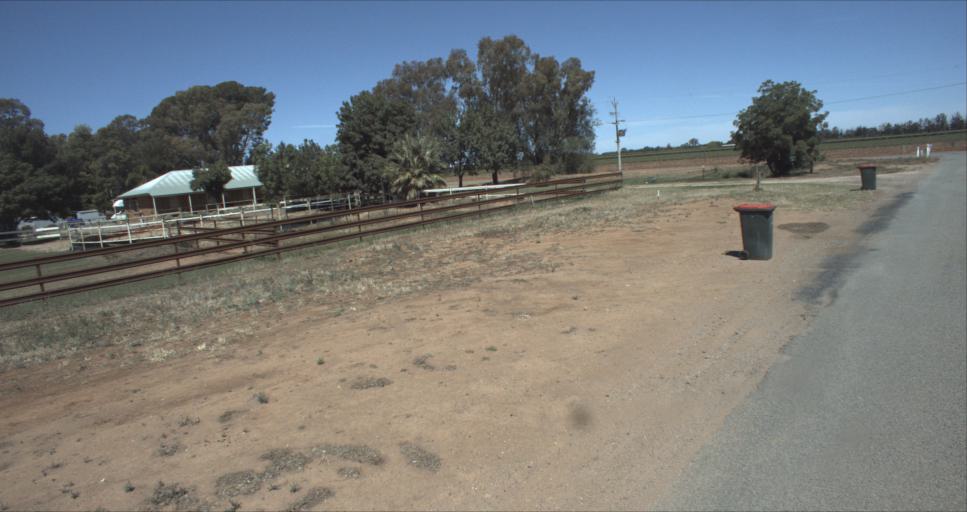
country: AU
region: New South Wales
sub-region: Leeton
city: Leeton
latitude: -34.5304
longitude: 146.3332
